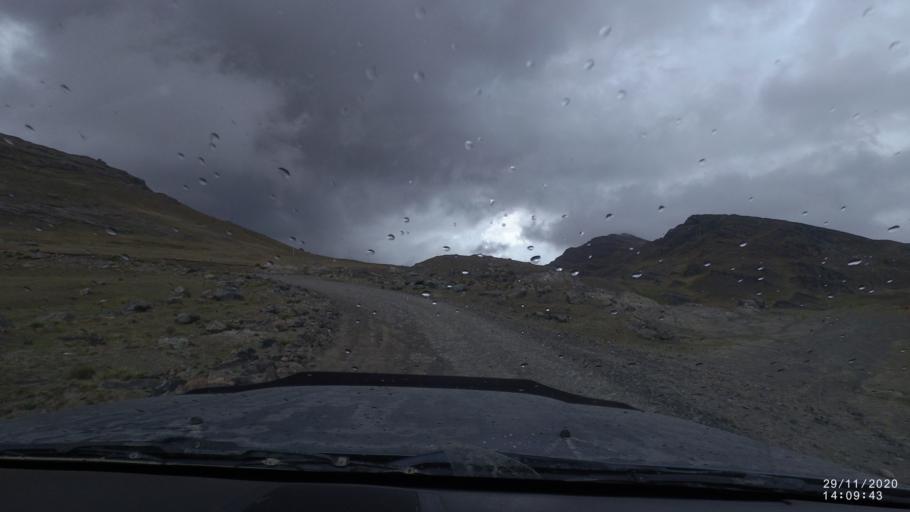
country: BO
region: Cochabamba
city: Sipe Sipe
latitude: -17.2282
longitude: -66.3871
